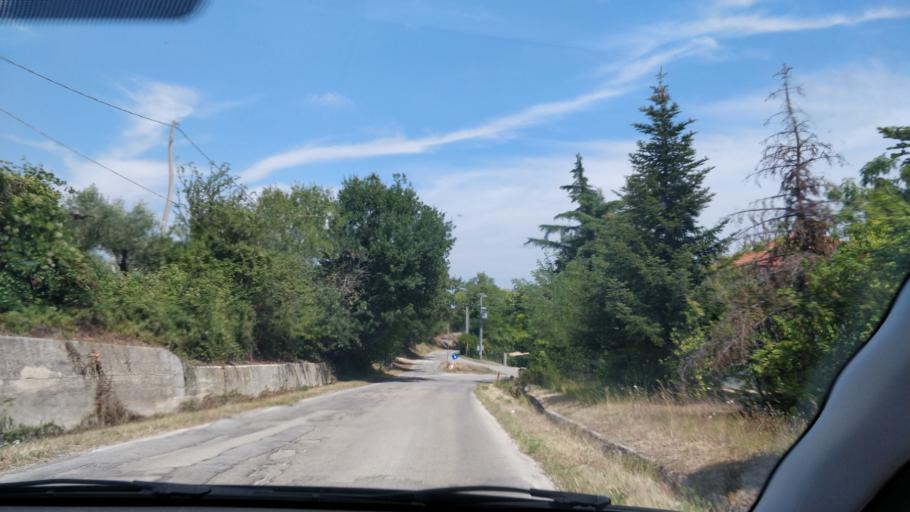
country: IT
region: Abruzzo
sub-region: Provincia di Chieti
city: Torrevecchia
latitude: 42.3972
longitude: 14.2009
